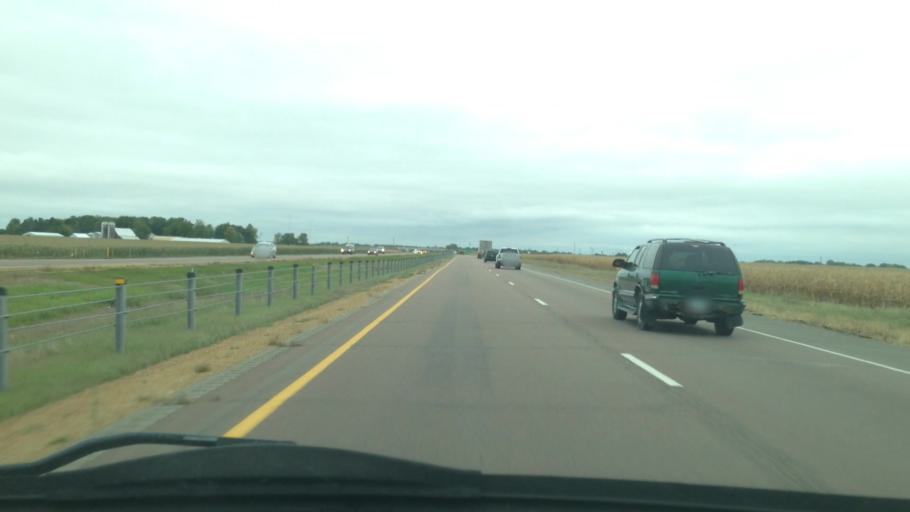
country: US
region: Minnesota
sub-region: Dakota County
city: Rosemount
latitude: 44.6967
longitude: -93.0246
